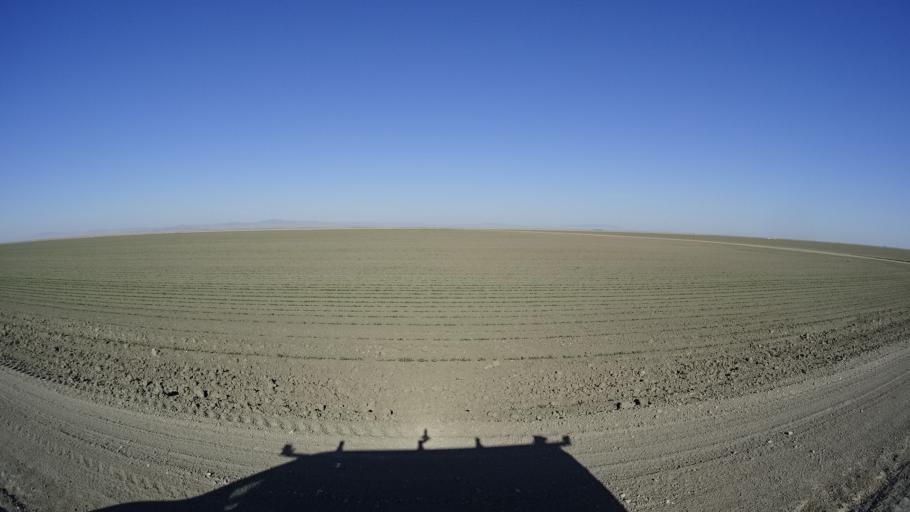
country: US
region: California
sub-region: Kings County
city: Stratford
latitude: 36.0935
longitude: -119.7978
